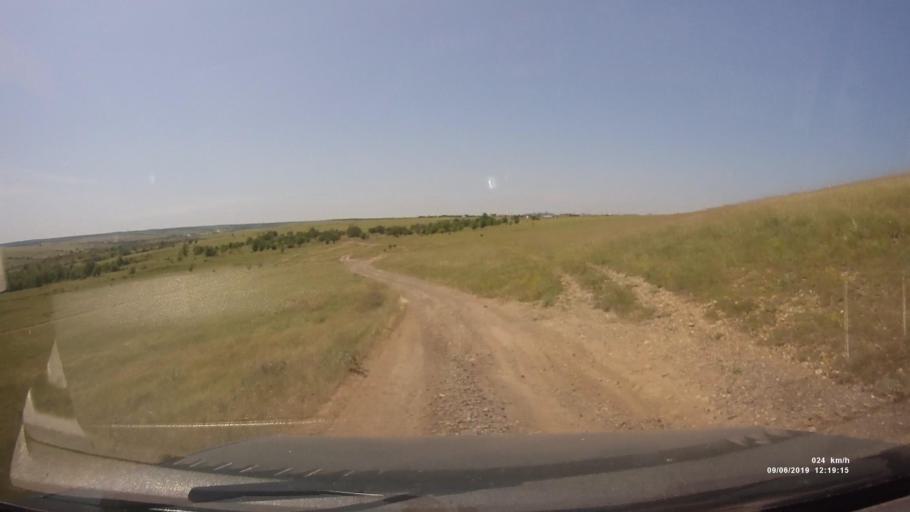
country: RU
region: Rostov
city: Kamensk-Shakhtinskiy
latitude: 48.2533
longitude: 40.3064
